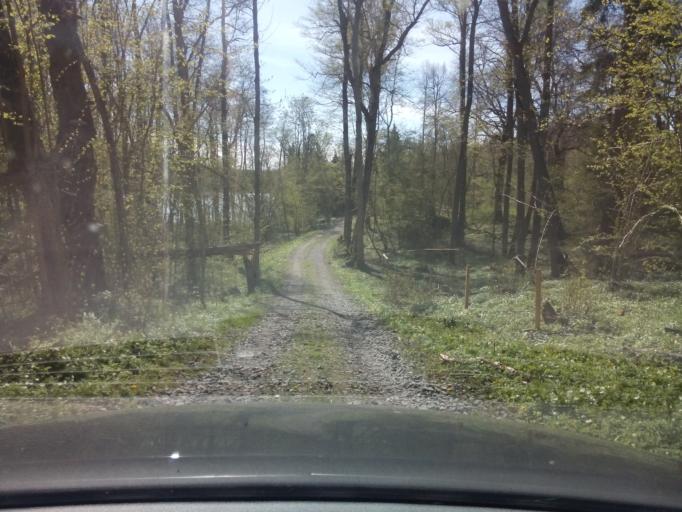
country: SE
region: Soedermanland
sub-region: Trosa Kommun
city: Trosa
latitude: 58.7888
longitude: 17.3743
